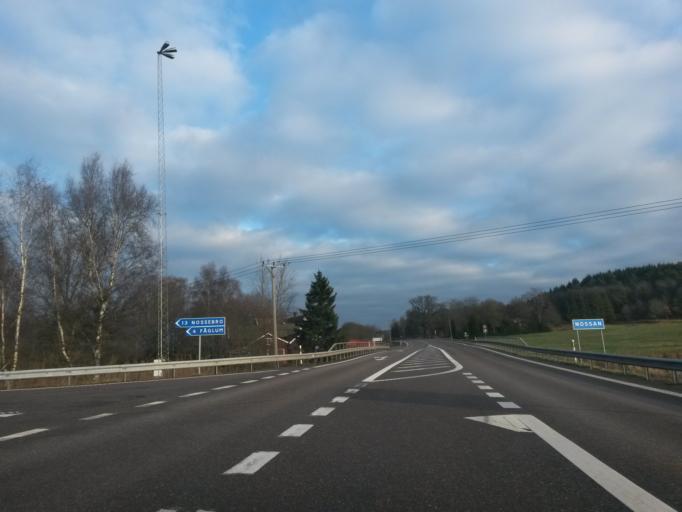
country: SE
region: Vaestra Goetaland
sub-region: Vargarda Kommun
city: Vargarda
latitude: 58.0994
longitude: 12.8330
